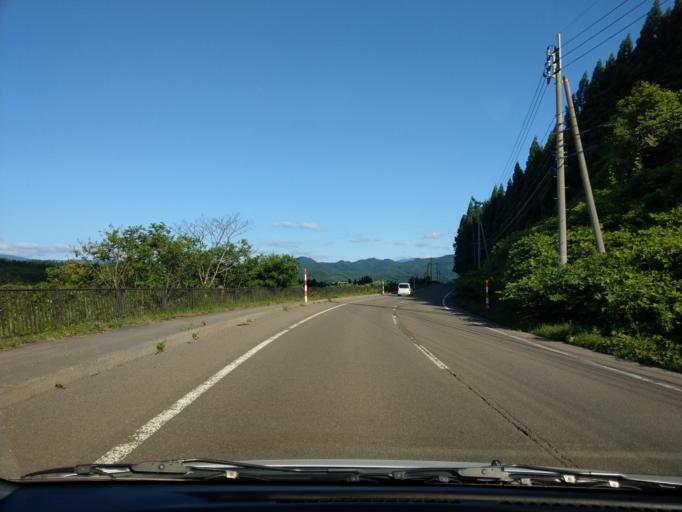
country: JP
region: Akita
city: Takanosu
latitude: 40.1179
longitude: 140.3886
